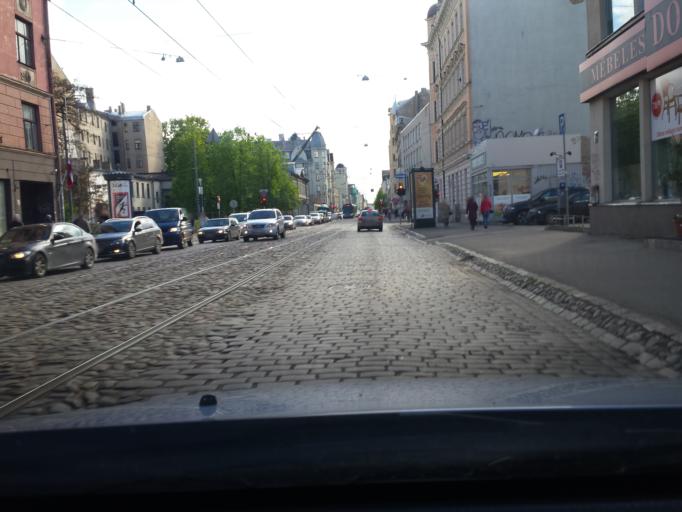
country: LV
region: Riga
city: Riga
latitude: 56.9568
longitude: 24.1324
